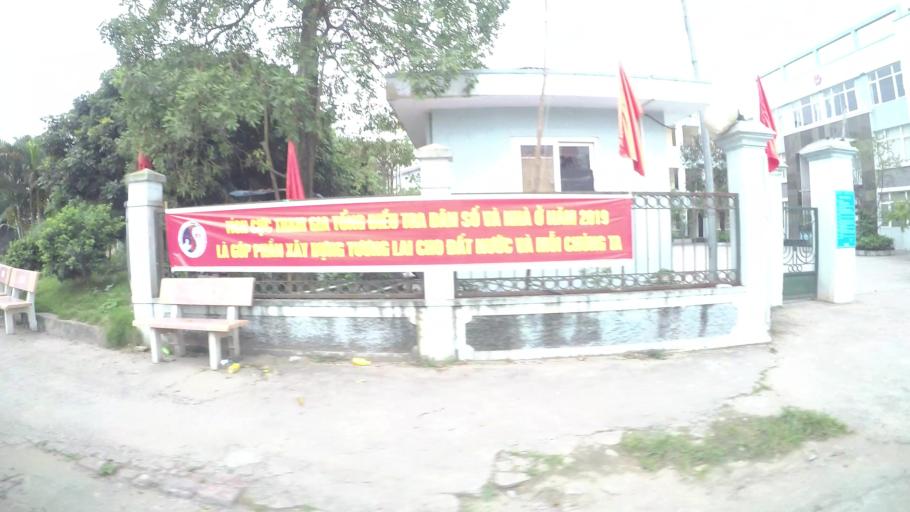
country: VN
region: Ha Noi
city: Trau Quy
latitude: 21.0450
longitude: 105.9298
